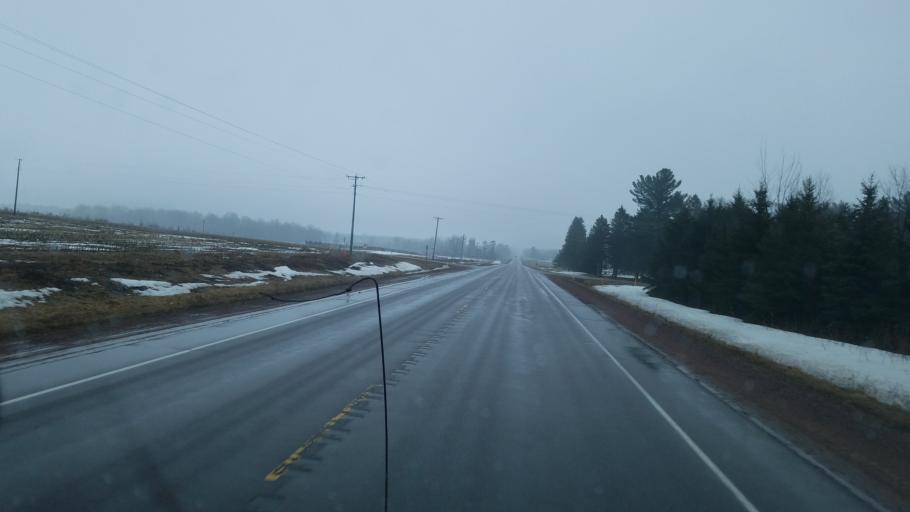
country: US
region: Wisconsin
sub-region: Wood County
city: Marshfield
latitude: 44.5986
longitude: -90.2398
